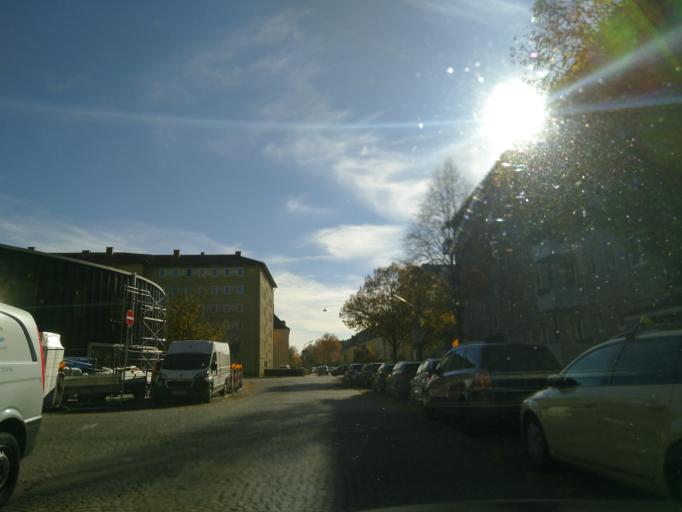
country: DE
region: Bavaria
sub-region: Upper Bavaria
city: Munich
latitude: 48.1059
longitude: 11.5910
